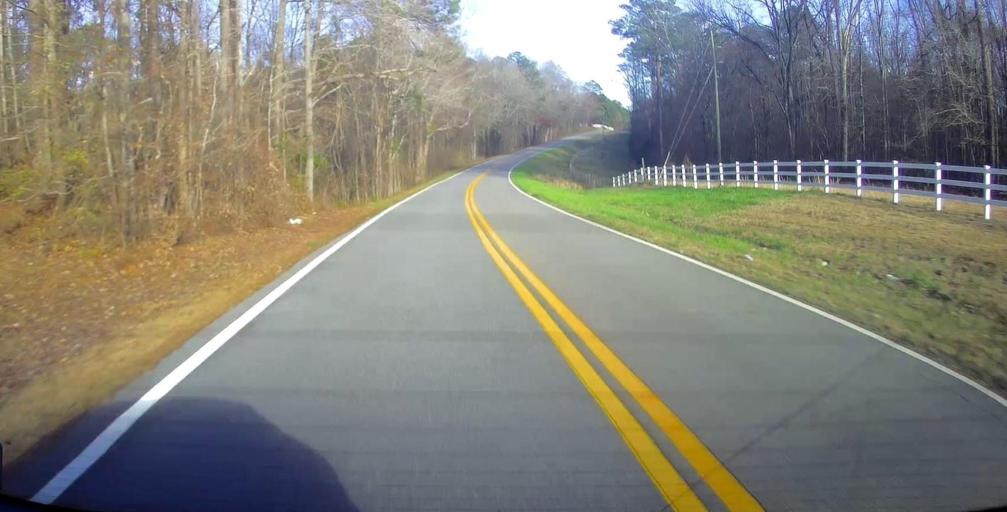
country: US
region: Georgia
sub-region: Bibb County
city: West Point
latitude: 32.8396
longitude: -83.9129
